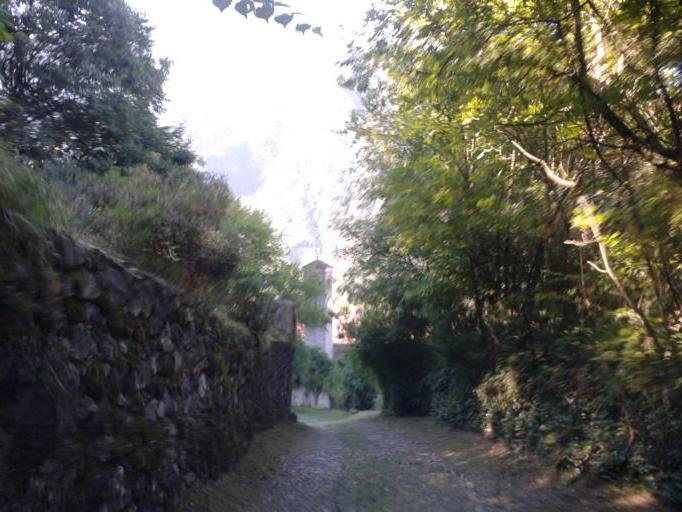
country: IT
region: Trentino-Alto Adige
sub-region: Provincia di Trento
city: Storo
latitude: 45.8517
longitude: 10.5800
